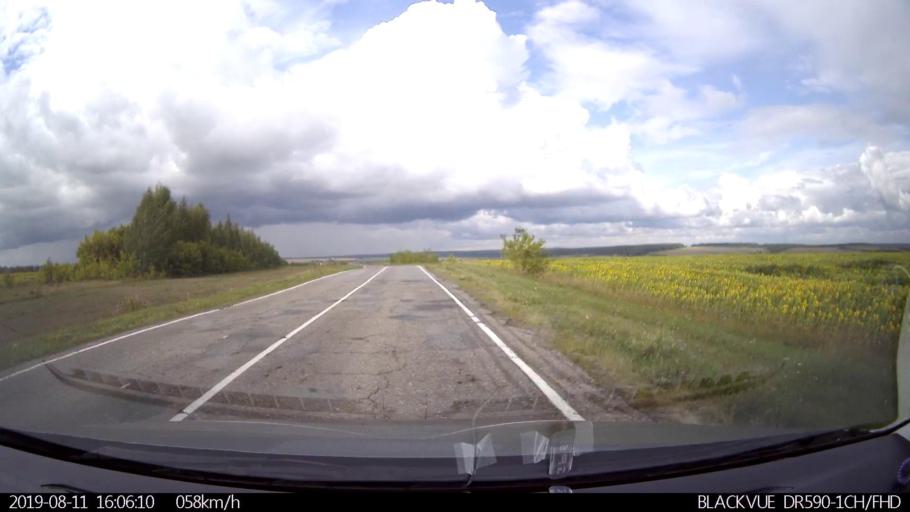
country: RU
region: Ulyanovsk
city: Ignatovka
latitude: 53.9663
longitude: 47.6492
